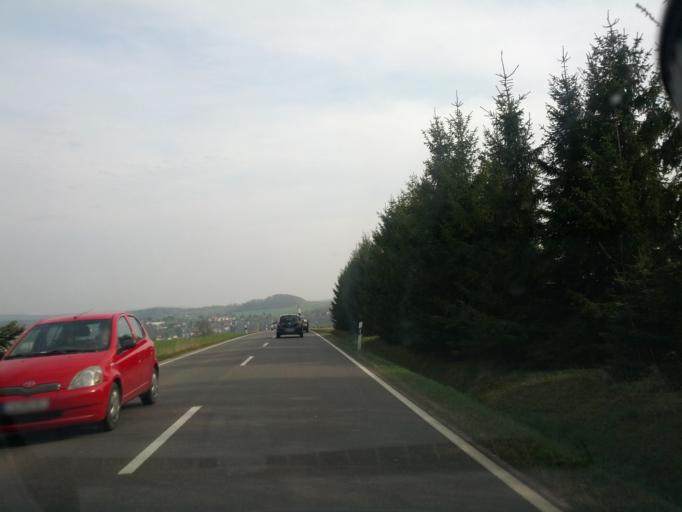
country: DE
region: Saxony
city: Wildenfels
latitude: 50.6758
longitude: 12.5921
